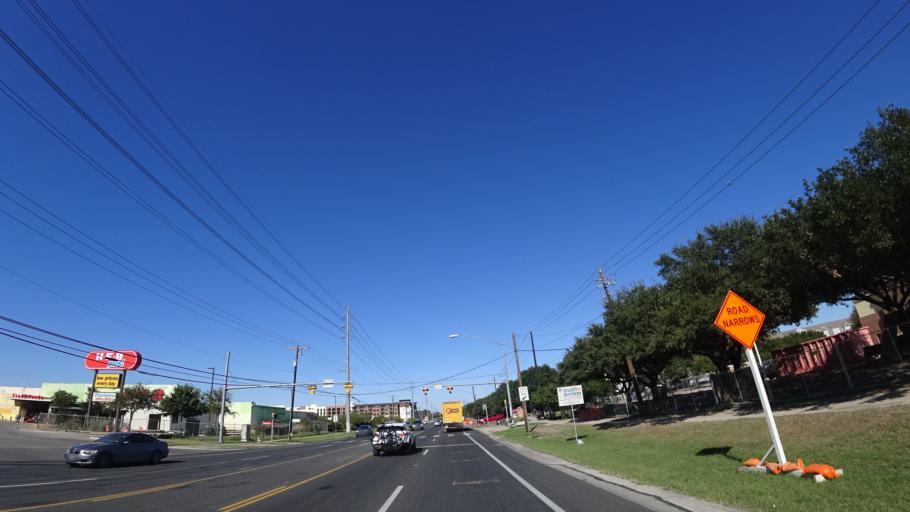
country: US
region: Texas
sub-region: Travis County
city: Austin
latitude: 30.2353
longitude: -97.7217
